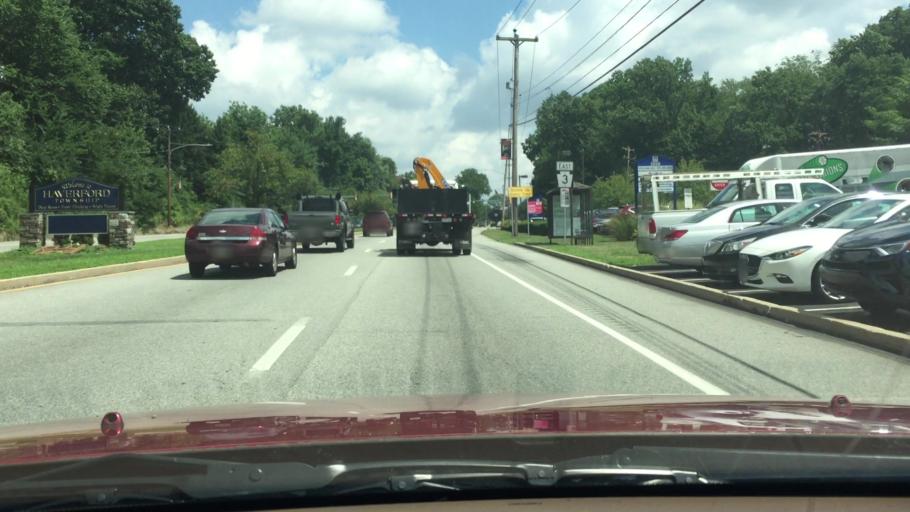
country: US
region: Pennsylvania
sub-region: Delaware County
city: Broomall
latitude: 39.9767
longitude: -75.3340
